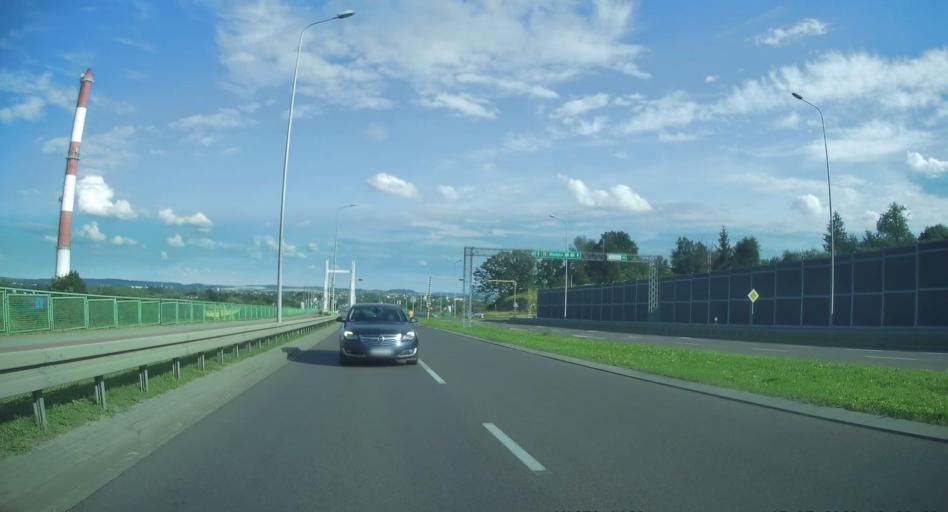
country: PL
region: Subcarpathian Voivodeship
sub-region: Przemysl
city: Przemysl
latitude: 49.8009
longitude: 22.7806
